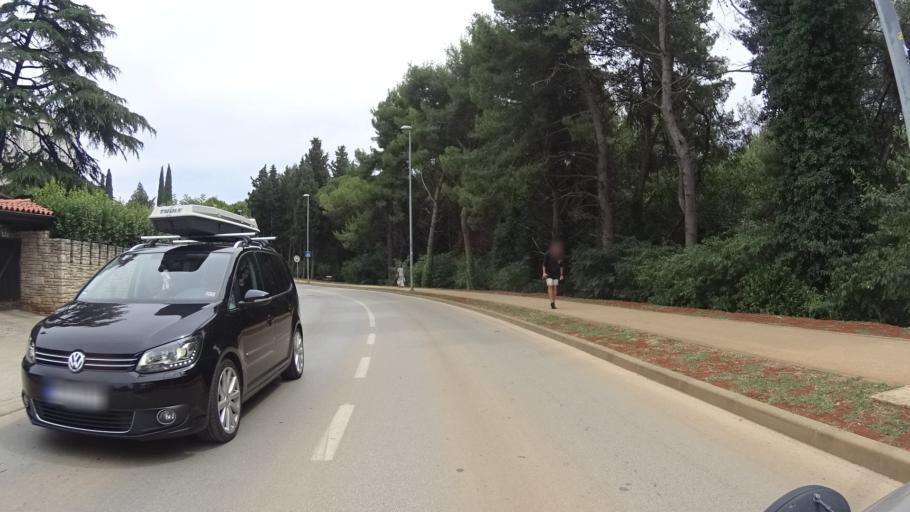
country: HR
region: Istarska
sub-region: Grad Pula
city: Pula
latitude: 44.8582
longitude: 13.8286
